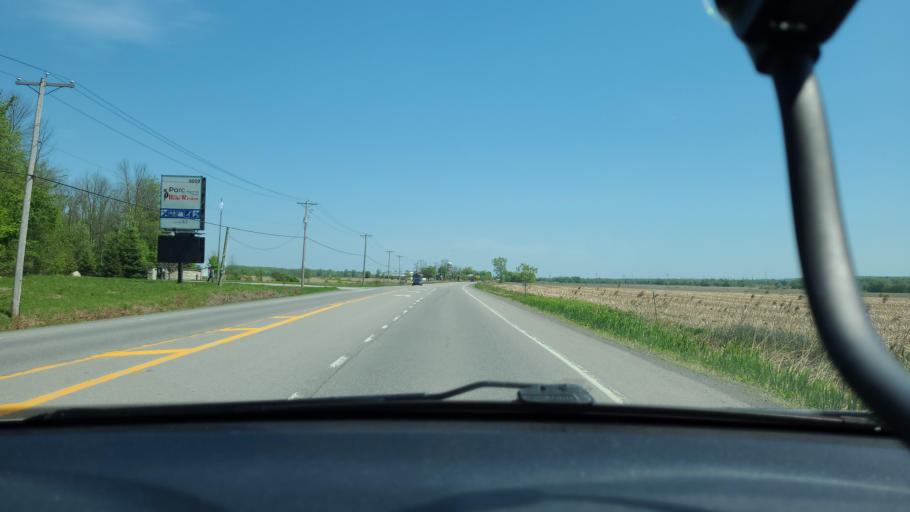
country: CA
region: Quebec
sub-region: Laurentides
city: Mirabel
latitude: 45.6178
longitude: -74.0960
